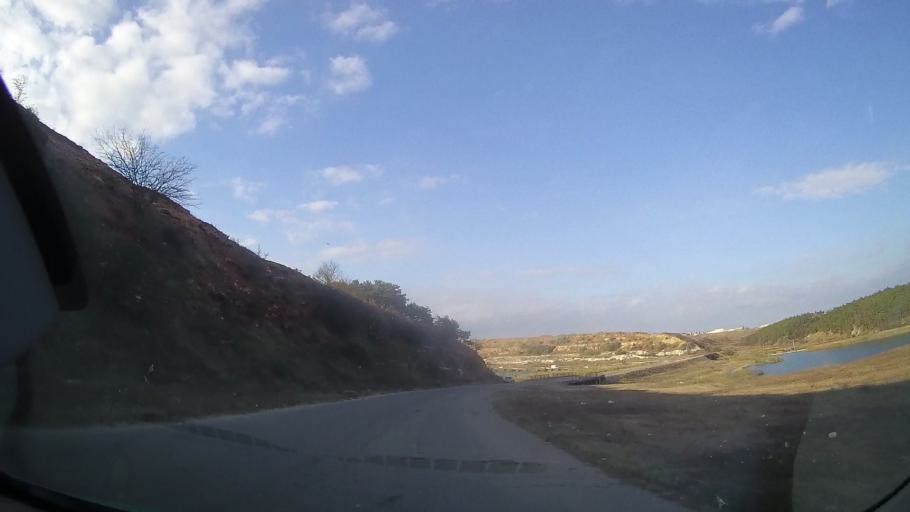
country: RO
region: Constanta
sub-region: Comuna Limanu
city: Limanu
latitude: 43.8112
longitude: 28.5173
